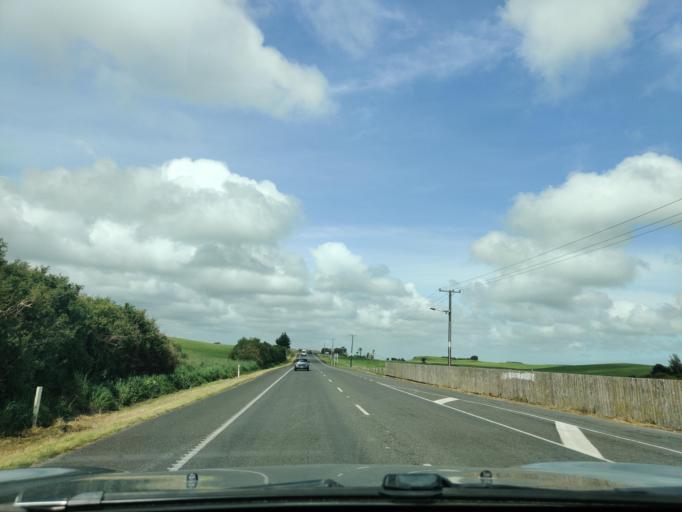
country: NZ
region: Taranaki
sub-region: South Taranaki District
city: Patea
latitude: -39.7701
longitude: 174.6646
